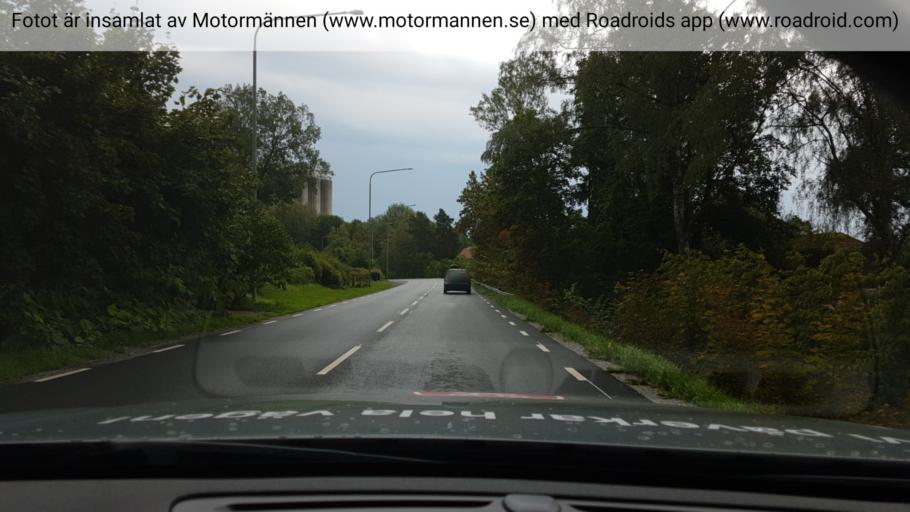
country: SE
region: Uppsala
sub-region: Habo Kommun
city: Balsta
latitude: 59.5545
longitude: 17.5466
